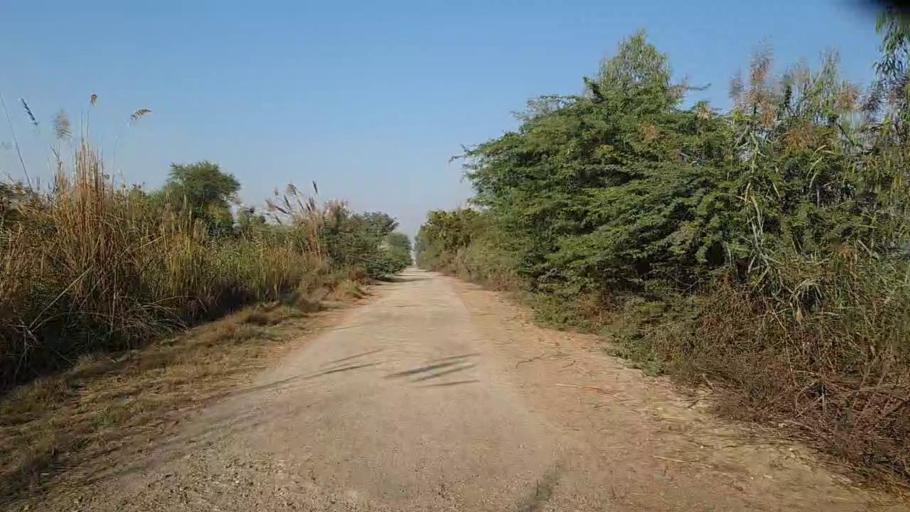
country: PK
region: Sindh
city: Ranipur
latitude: 27.2475
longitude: 68.5053
